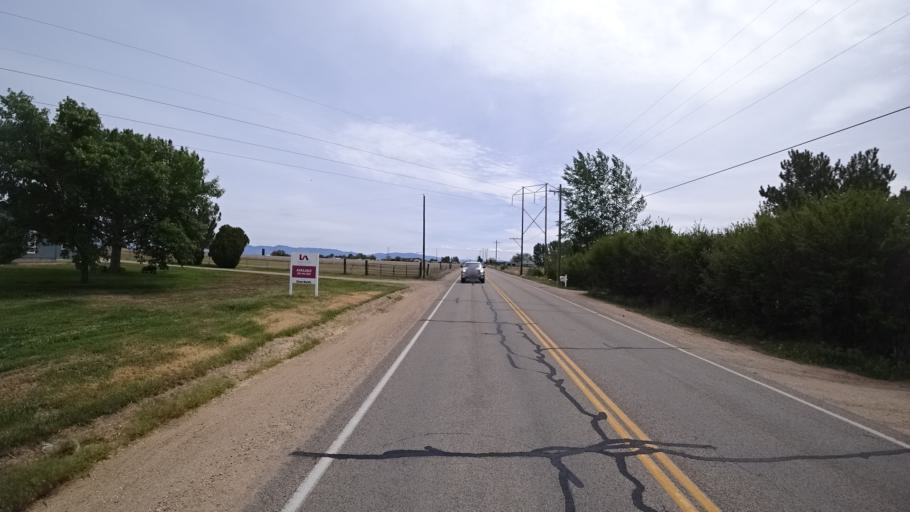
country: US
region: Idaho
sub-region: Ada County
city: Meridian
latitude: 43.5612
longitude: -116.4382
